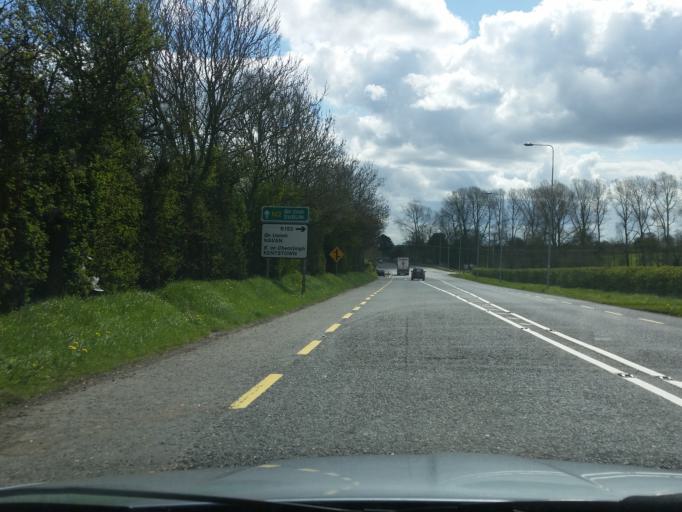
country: IE
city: Kentstown
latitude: 53.6247
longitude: -6.4887
